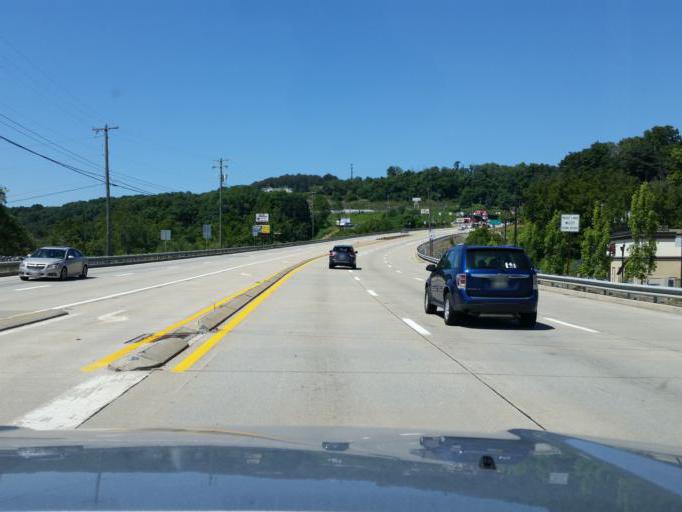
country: US
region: Pennsylvania
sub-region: Westmoreland County
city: Murrysville
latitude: 40.4271
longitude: -79.7009
